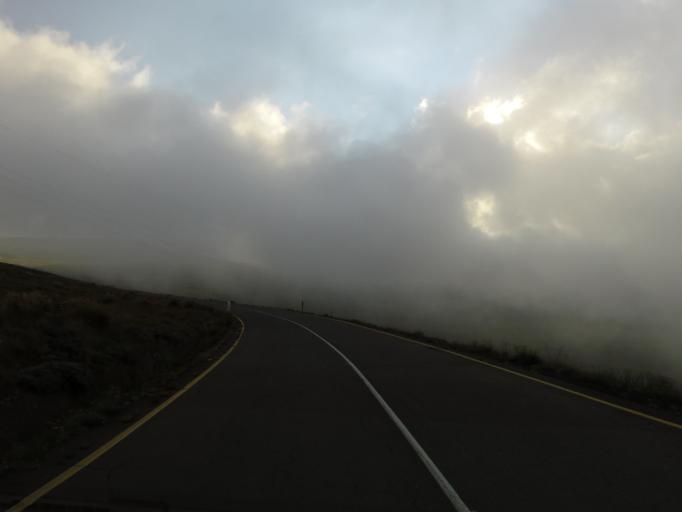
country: LS
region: Butha-Buthe
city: Butha-Buthe
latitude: -29.0660
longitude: 28.4144
